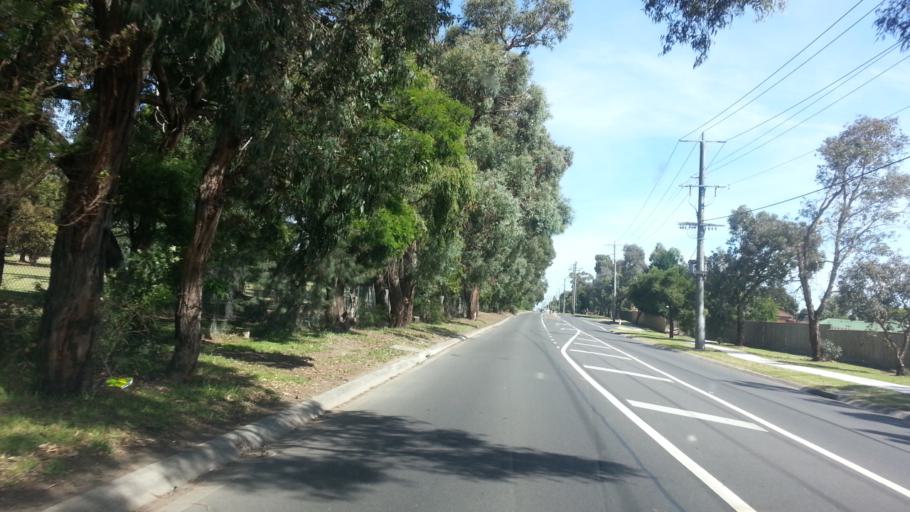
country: AU
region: Victoria
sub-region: Knox
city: Rowville
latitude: -37.9400
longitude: 145.2431
